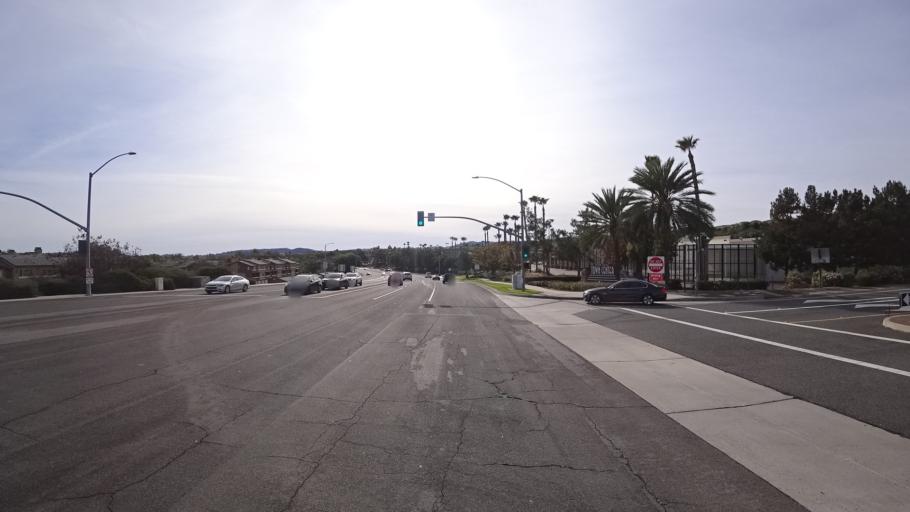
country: US
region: California
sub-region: Orange County
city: Aliso Viejo
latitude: 33.5795
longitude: -117.7221
